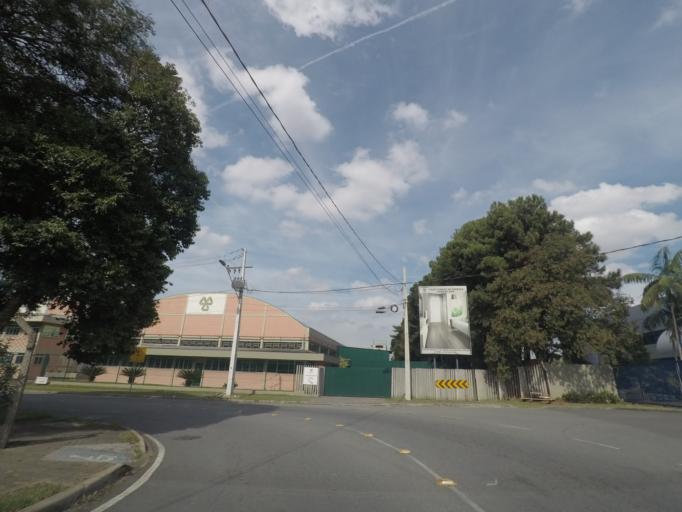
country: BR
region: Parana
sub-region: Curitiba
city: Curitiba
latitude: -25.4880
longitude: -49.2651
